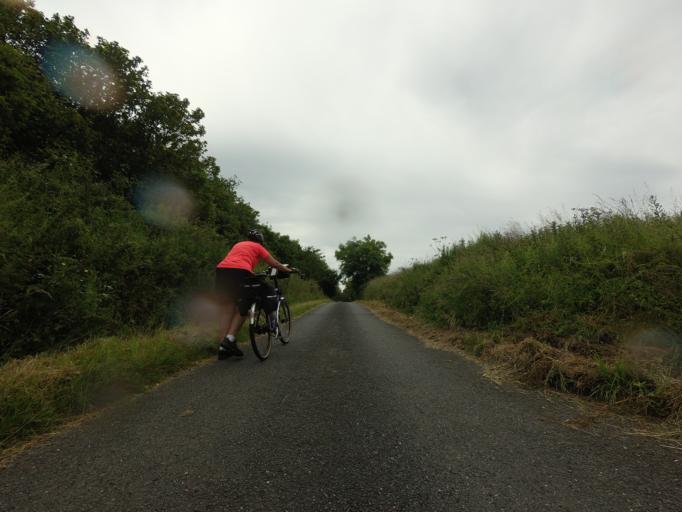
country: GB
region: Scotland
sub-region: Aberdeenshire
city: Portsoy
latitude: 57.6762
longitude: -2.6575
